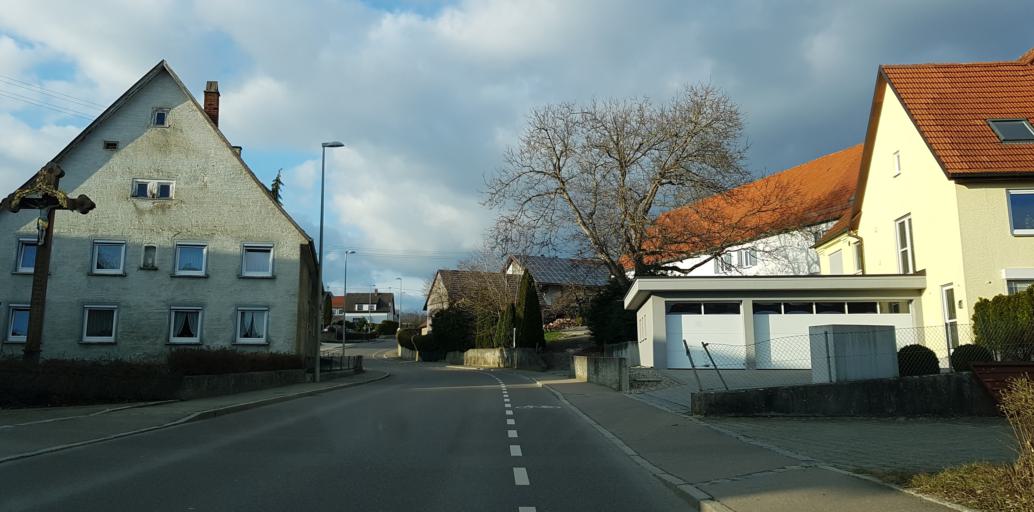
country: DE
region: Baden-Wuerttemberg
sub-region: Tuebingen Region
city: Erbach
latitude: 48.3643
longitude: 9.8788
